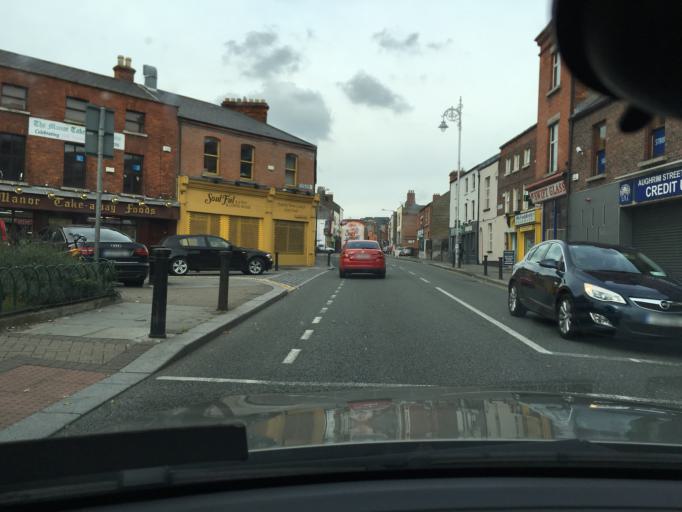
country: IE
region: Leinster
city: Cabra
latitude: 53.3534
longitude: -6.2854
